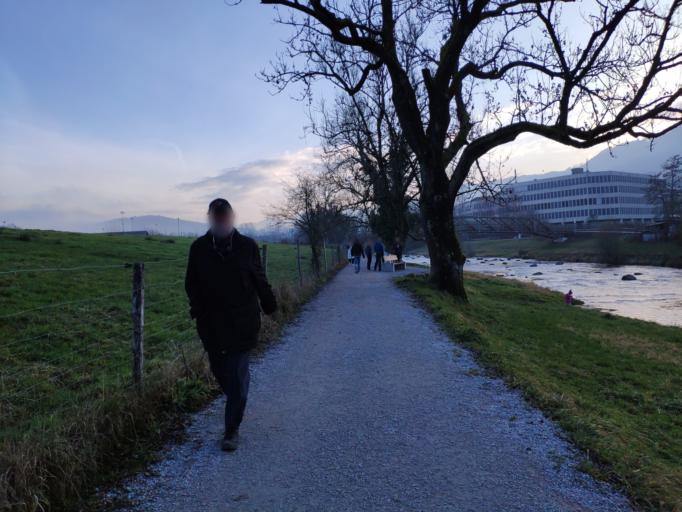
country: CH
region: Zurich
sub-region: Bezirk Horgen
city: Adliswil / Sood
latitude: 47.3229
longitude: 8.5247
